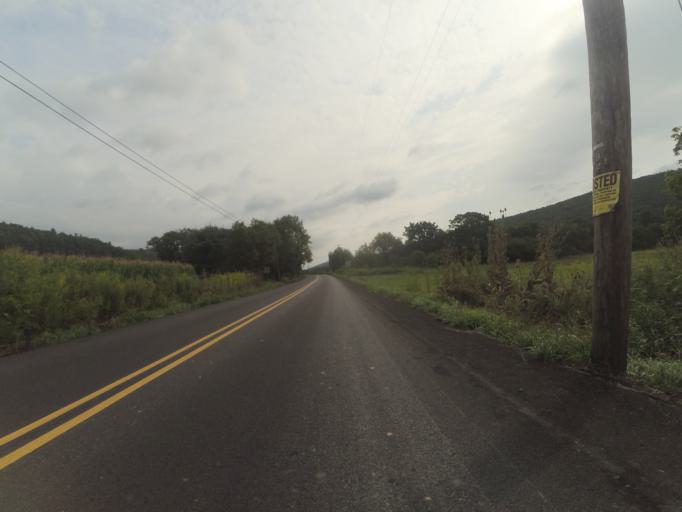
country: US
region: Pennsylvania
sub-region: Centre County
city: Milesburg
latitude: 41.0441
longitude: -77.7136
